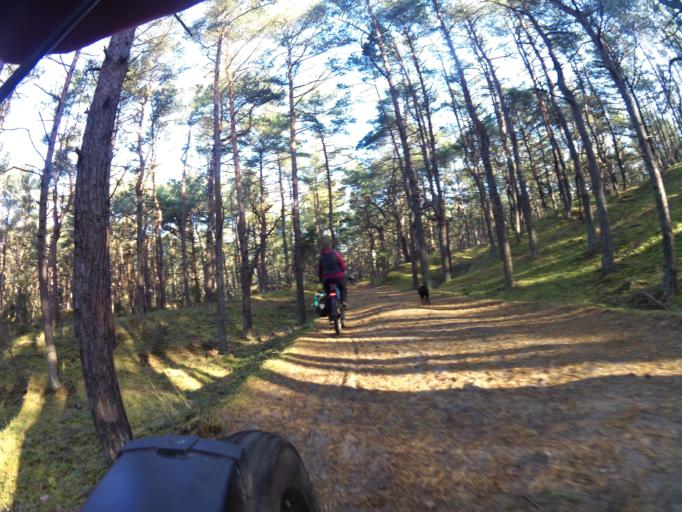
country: PL
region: Pomeranian Voivodeship
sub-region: Powiat pucki
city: Hel
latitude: 54.5973
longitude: 18.8128
